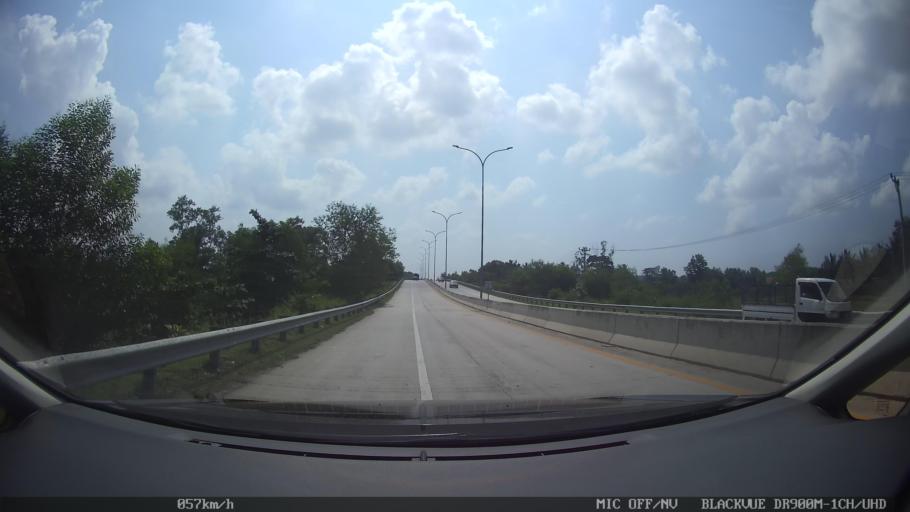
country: ID
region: Lampung
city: Natar
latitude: -5.2812
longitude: 105.1963
